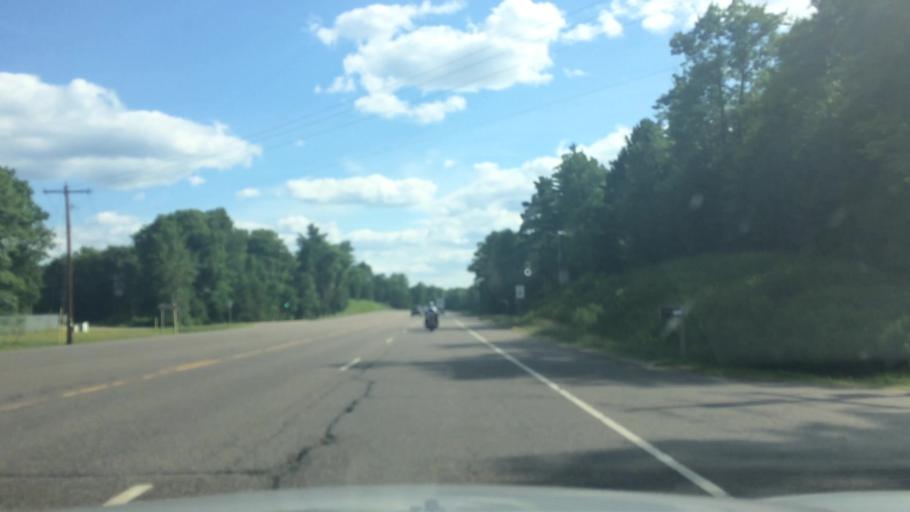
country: US
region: Wisconsin
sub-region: Vilas County
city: Lac du Flambeau
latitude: 45.8432
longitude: -89.7065
